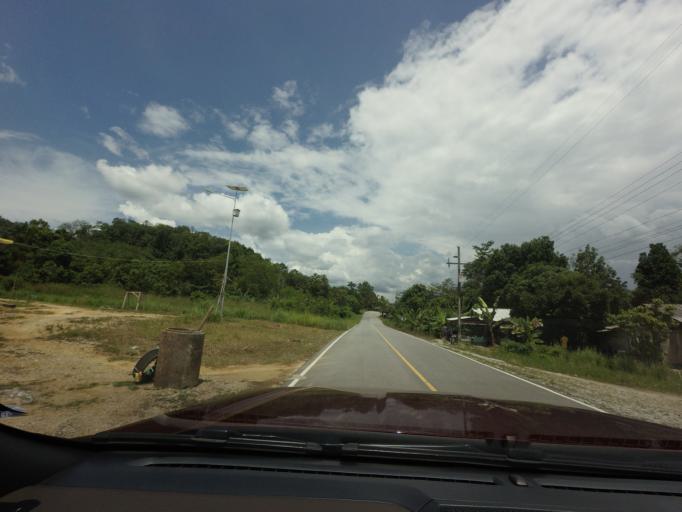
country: TH
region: Narathiwat
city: Chanae
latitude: 6.0717
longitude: 101.6874
